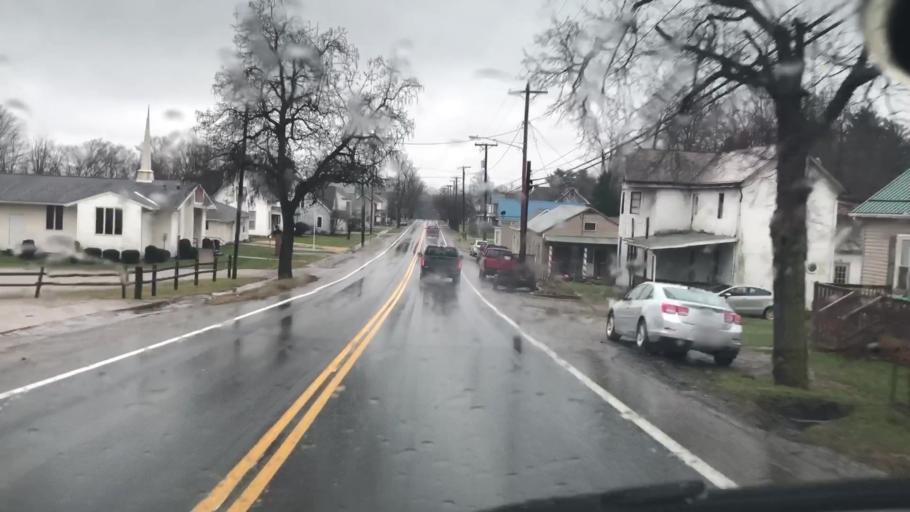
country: US
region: Ohio
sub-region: Harrison County
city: Cadiz
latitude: 40.1828
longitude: -80.9959
